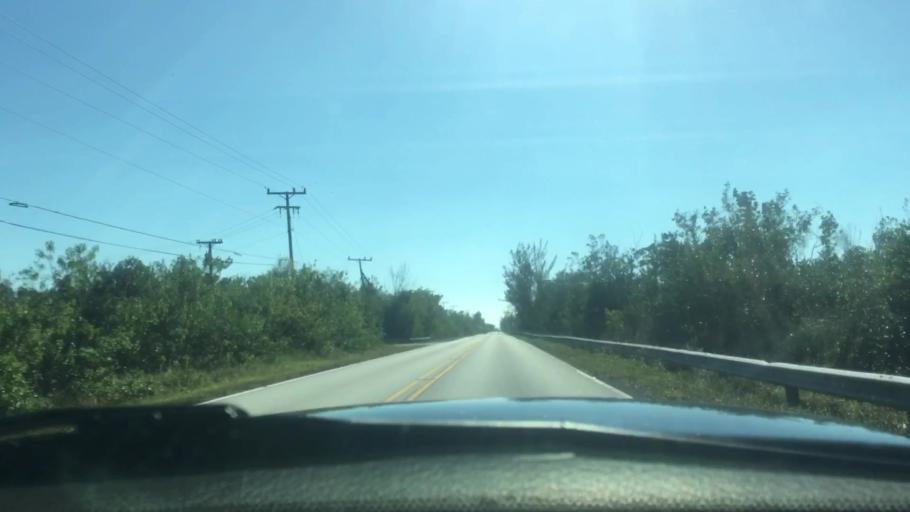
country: US
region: Florida
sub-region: Miami-Dade County
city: Florida City
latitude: 25.3731
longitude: -80.4339
